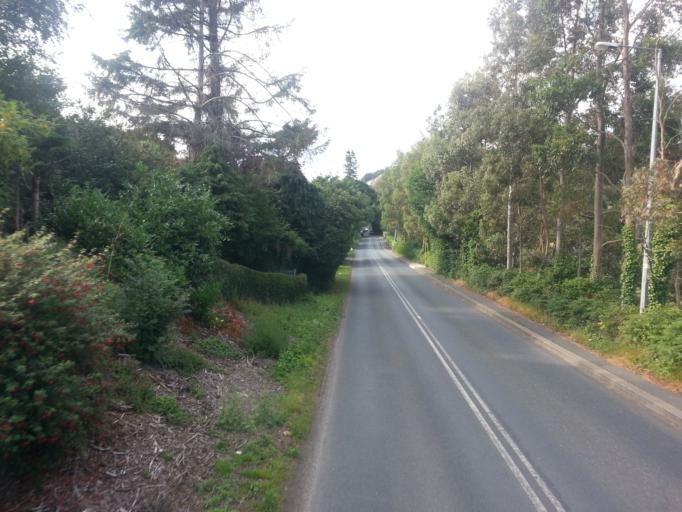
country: IE
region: Leinster
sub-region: Wicklow
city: Enniskerry
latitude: 53.2096
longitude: -6.1750
